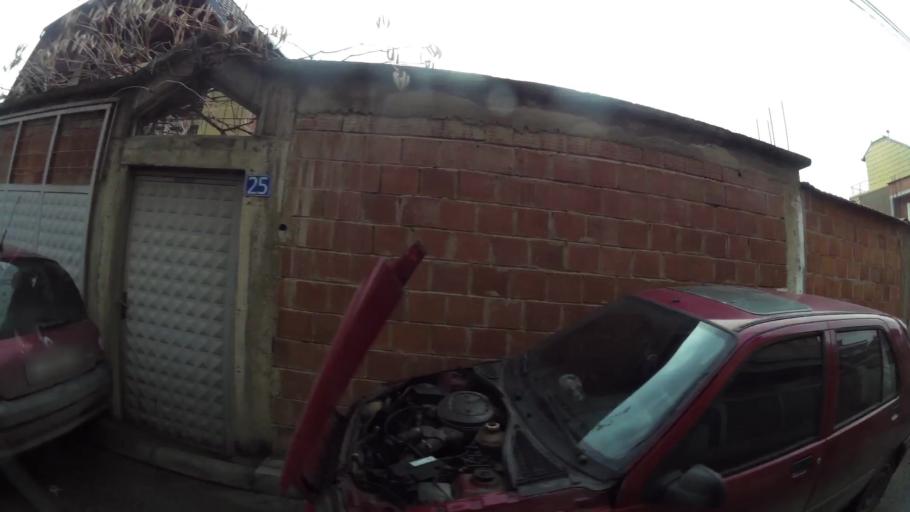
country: XK
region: Pristina
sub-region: Komuna e Prishtines
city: Pristina
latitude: 42.6723
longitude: 21.1606
